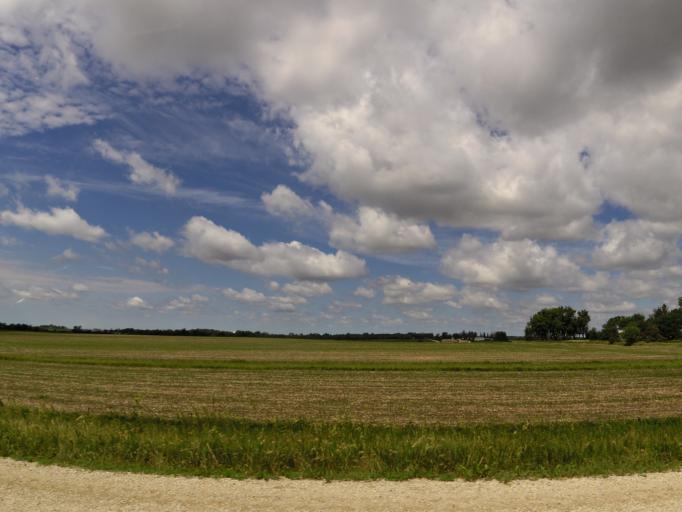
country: US
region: Iowa
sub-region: Chickasaw County
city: New Hampton
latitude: 43.1036
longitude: -92.2979
